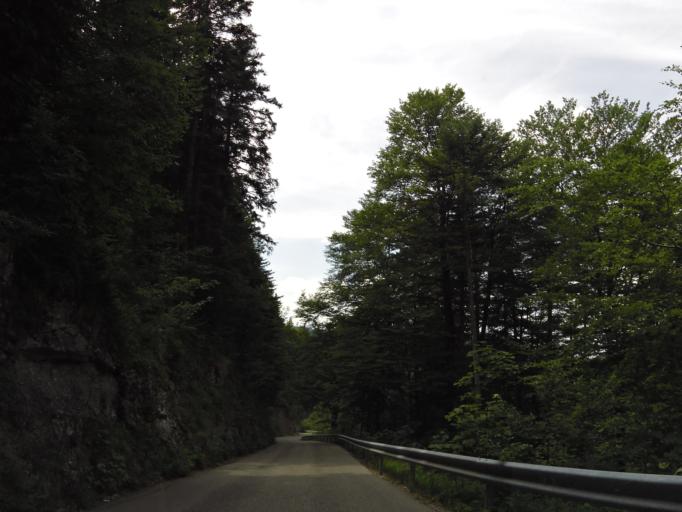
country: AT
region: Tyrol
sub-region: Politischer Bezirk Kitzbuhel
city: Waidring
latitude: 47.6603
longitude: 12.5526
